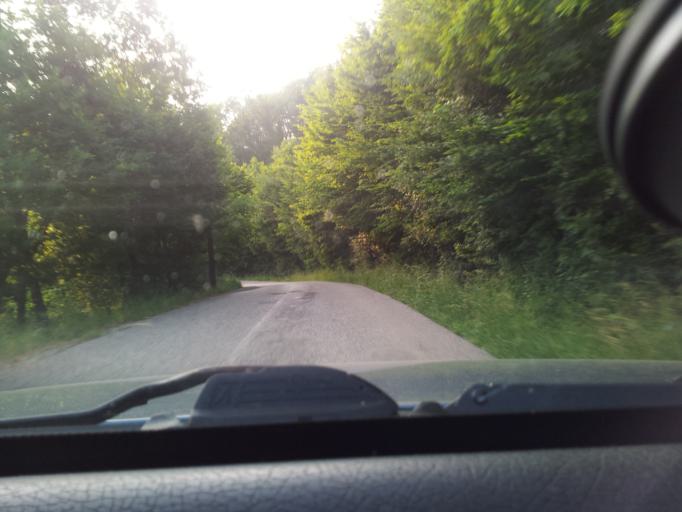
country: SK
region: Banskobystricky
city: Zarnovica
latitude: 48.3756
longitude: 18.7527
